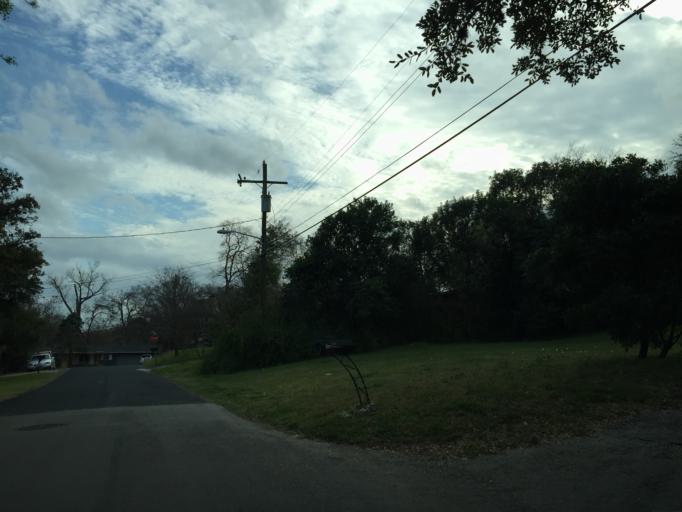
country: US
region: Texas
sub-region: Travis County
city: Wells Branch
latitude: 30.3849
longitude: -97.6784
